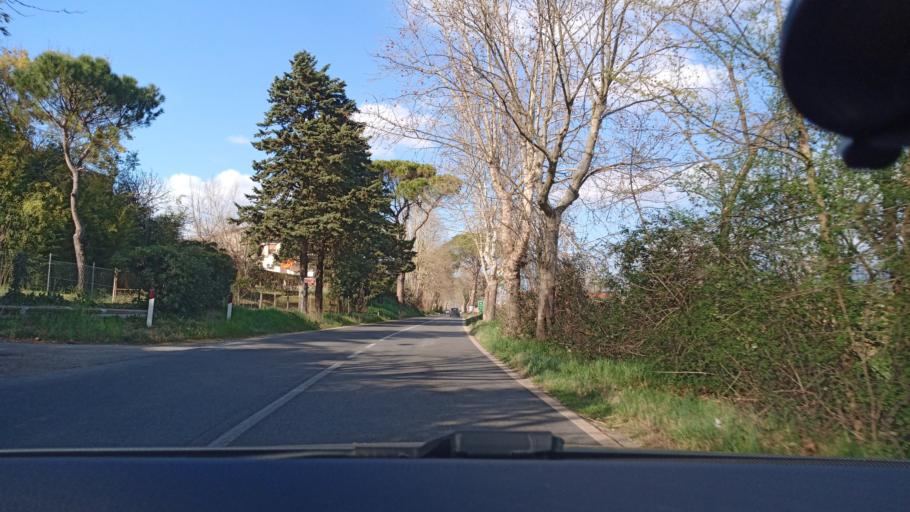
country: IT
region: Latium
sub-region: Citta metropolitana di Roma Capitale
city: Torrita Tiberina
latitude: 42.2507
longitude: 12.6367
